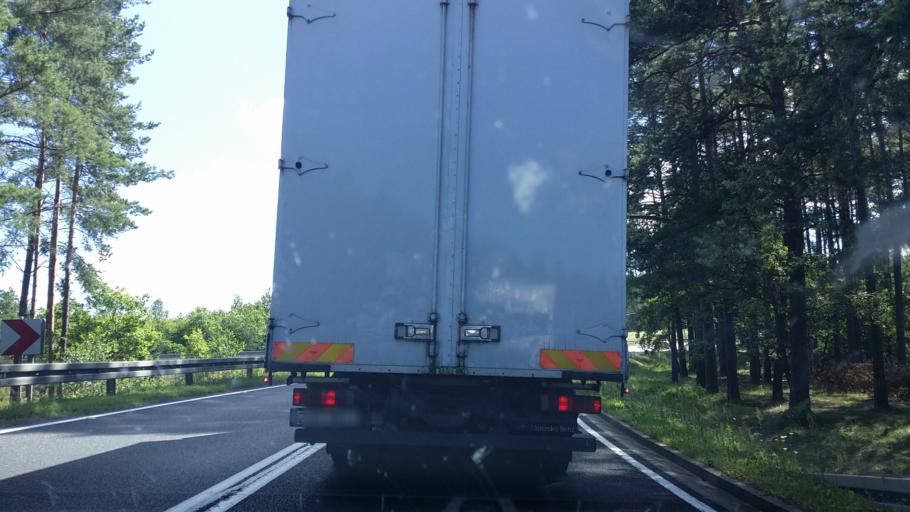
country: PL
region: West Pomeranian Voivodeship
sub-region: Powiat choszczenski
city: Drawno
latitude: 53.3045
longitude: 15.7844
